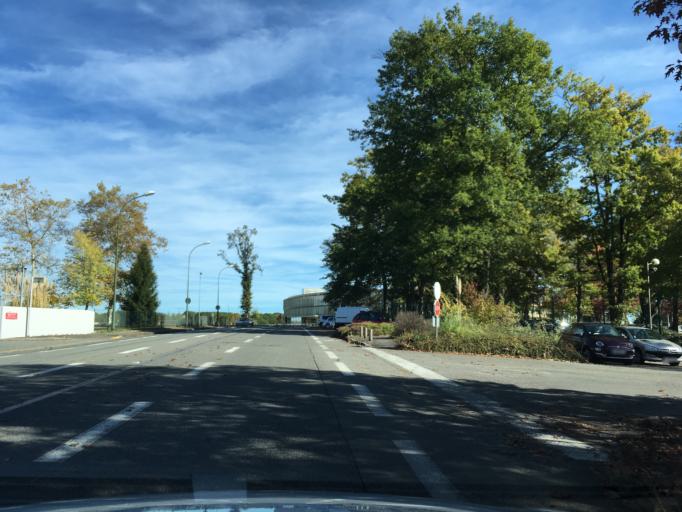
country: FR
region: Aquitaine
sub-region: Departement des Pyrenees-Atlantiques
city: Buros
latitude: 43.3209
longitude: -0.3133
